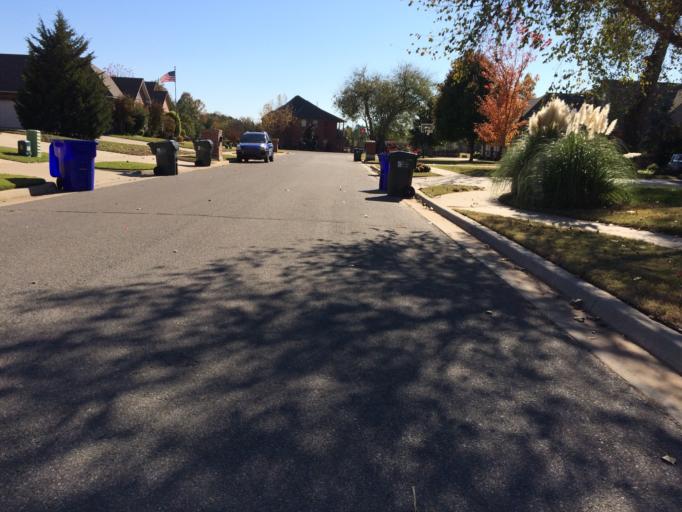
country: US
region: Oklahoma
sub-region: Cleveland County
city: Noble
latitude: 35.1655
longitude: -97.4198
